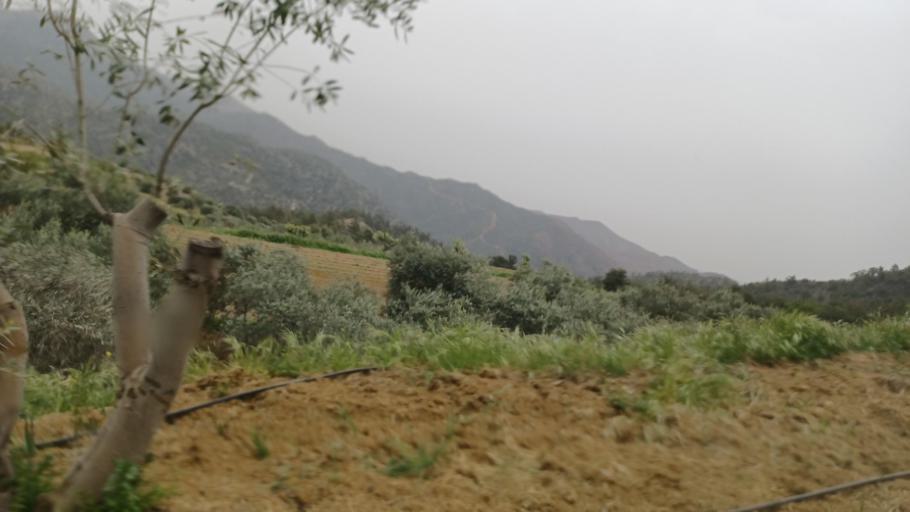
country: CY
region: Limassol
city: Parekklisha
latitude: 34.8604
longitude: 33.0958
